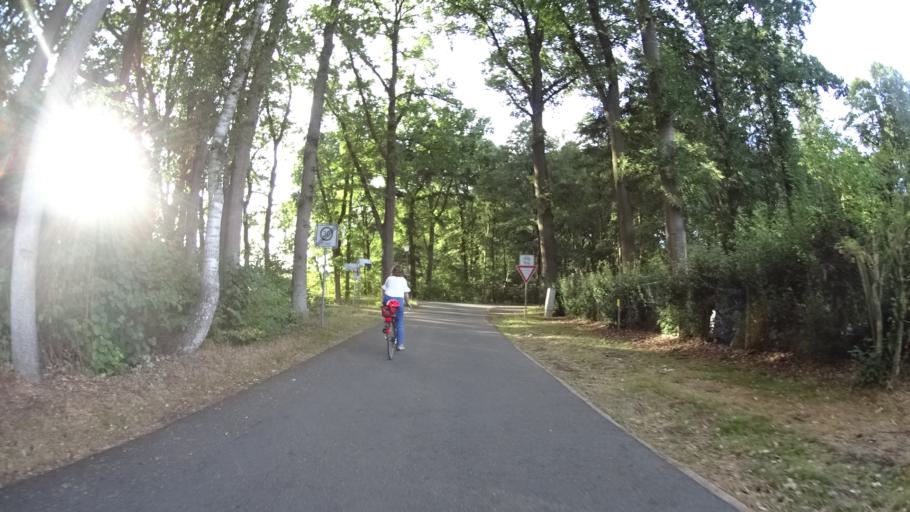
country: DE
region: Lower Saxony
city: Handeloh
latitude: 53.2379
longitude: 9.8638
